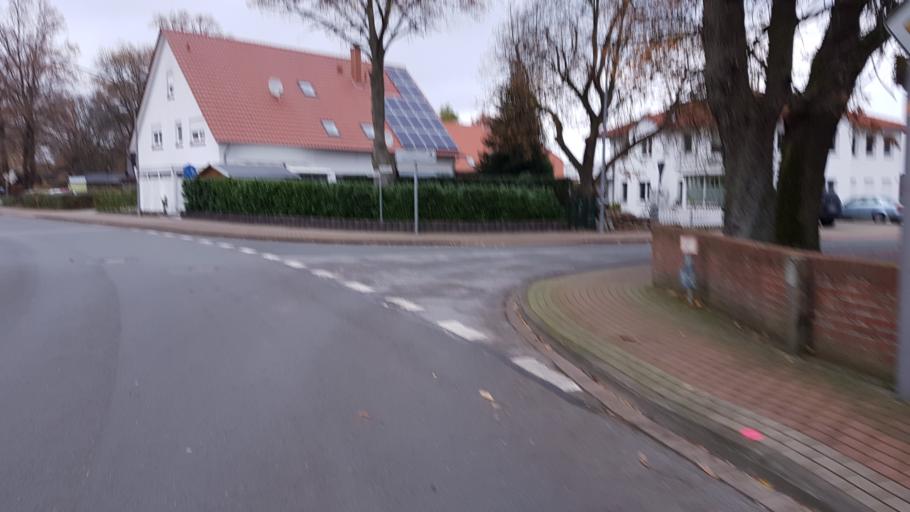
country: DE
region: North Rhine-Westphalia
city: Rahden
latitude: 52.4380
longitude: 8.6130
